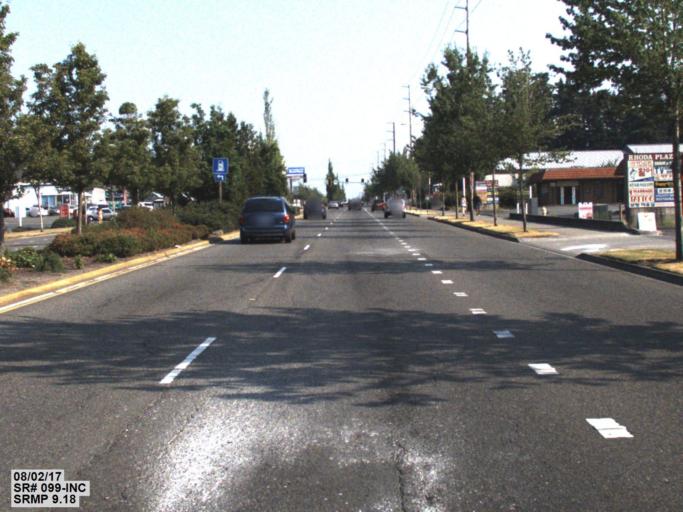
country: US
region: Washington
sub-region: King County
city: Federal Way
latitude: 47.3042
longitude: -122.3133
